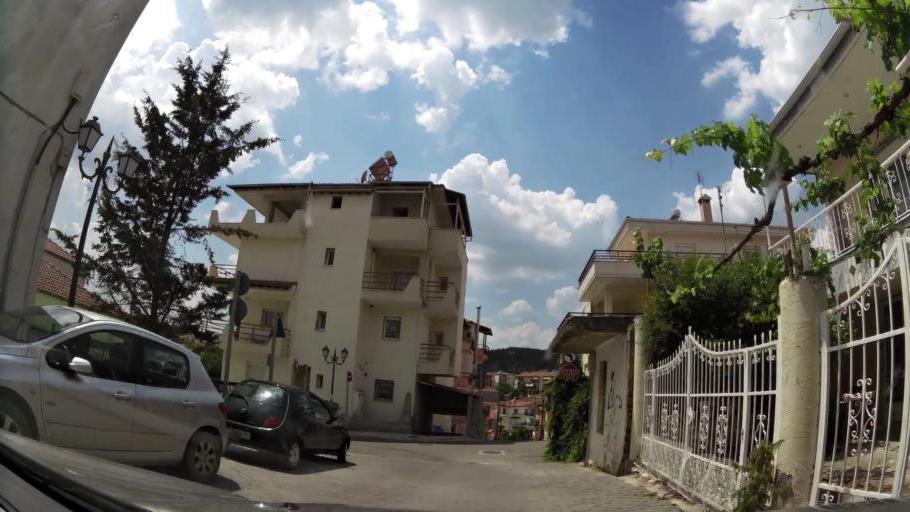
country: GR
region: West Macedonia
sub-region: Nomos Kozanis
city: Kozani
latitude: 40.3059
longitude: 21.7917
